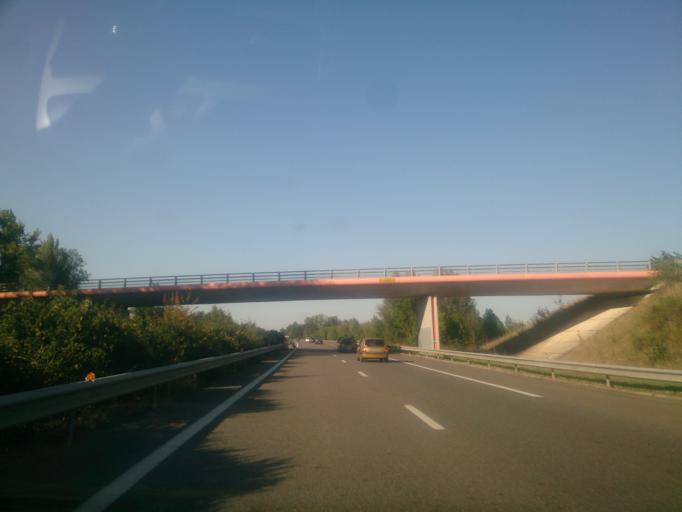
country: FR
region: Midi-Pyrenees
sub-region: Departement du Tarn-et-Garonne
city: Realville
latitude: 44.1175
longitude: 1.4733
